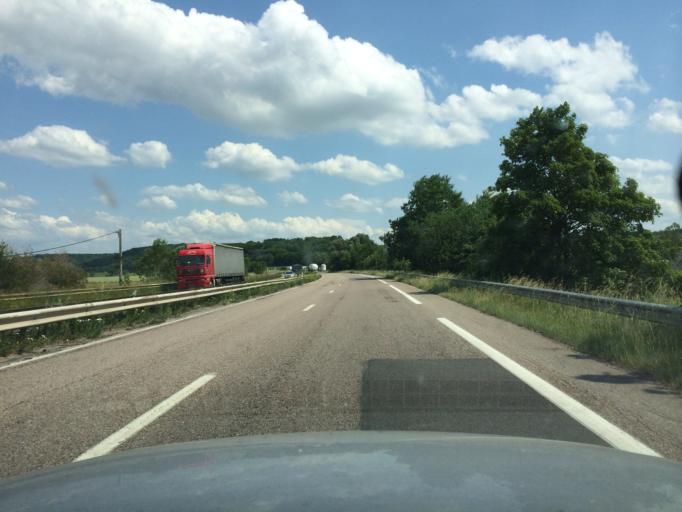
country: FR
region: Lorraine
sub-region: Departement de la Meuse
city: Vacon
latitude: 48.6887
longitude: 5.6288
